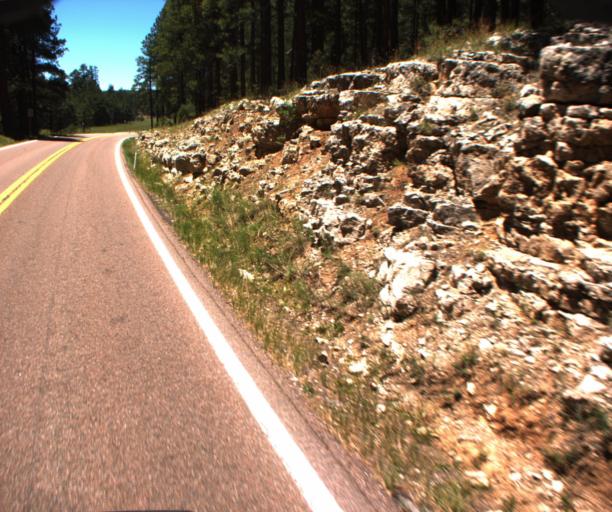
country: US
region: Arizona
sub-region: Gila County
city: Pine
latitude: 34.5396
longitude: -111.3284
